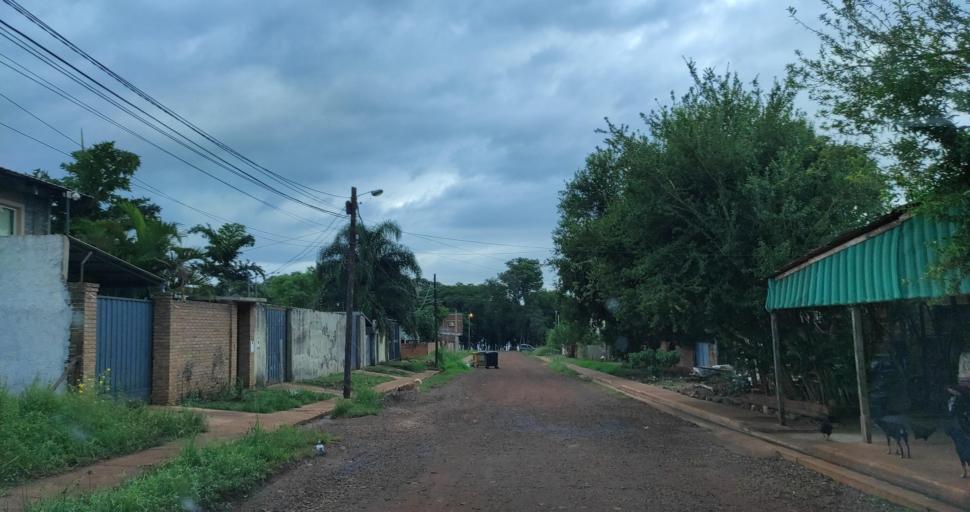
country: AR
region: Misiones
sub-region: Departamento de Capital
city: Posadas
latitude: -27.3638
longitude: -55.9455
